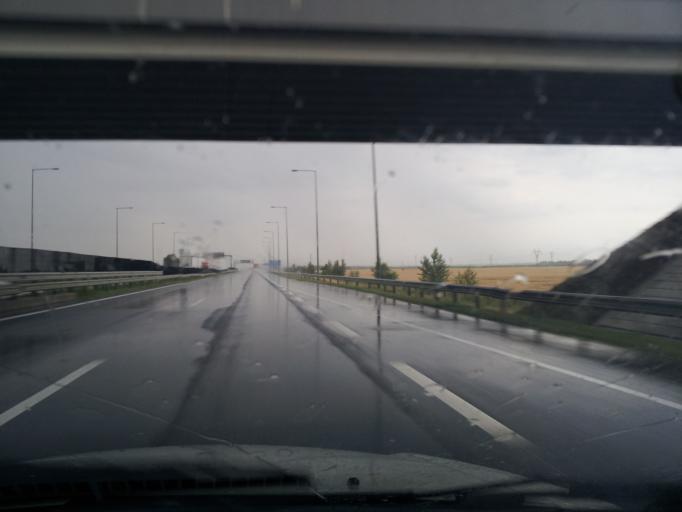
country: HU
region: Borsod-Abauj-Zemplen
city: Alsozsolca
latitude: 48.0561
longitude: 20.8477
